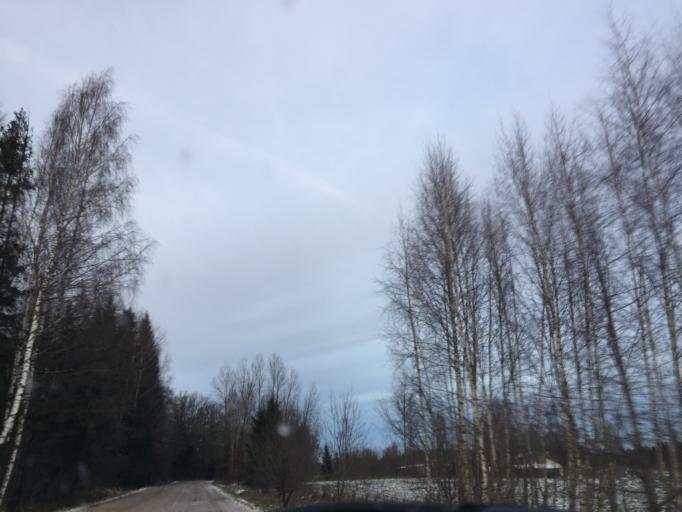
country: LV
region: Limbazu Rajons
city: Limbazi
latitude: 57.5575
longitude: 24.8162
